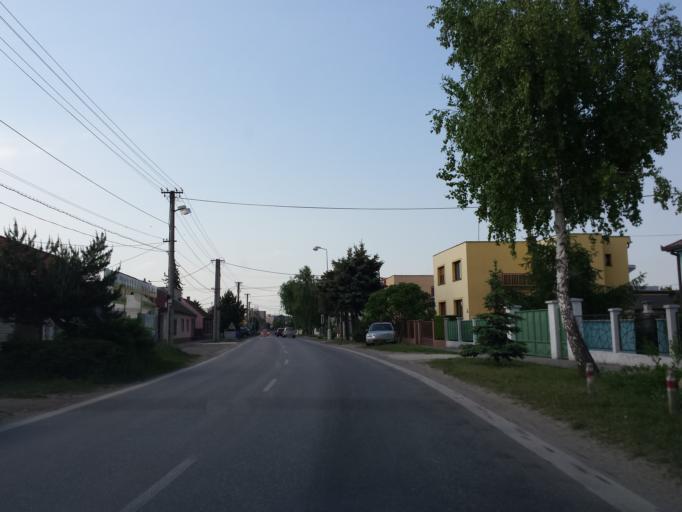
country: SK
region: Bratislavsky
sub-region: Okres Malacky
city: Malacky
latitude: 48.4283
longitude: 17.0210
